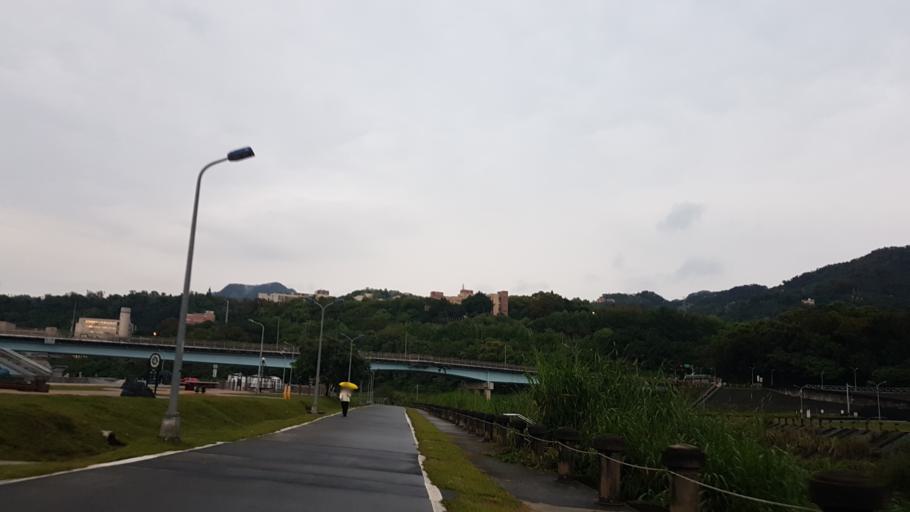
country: TW
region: Taipei
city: Taipei
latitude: 24.9813
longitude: 121.5659
